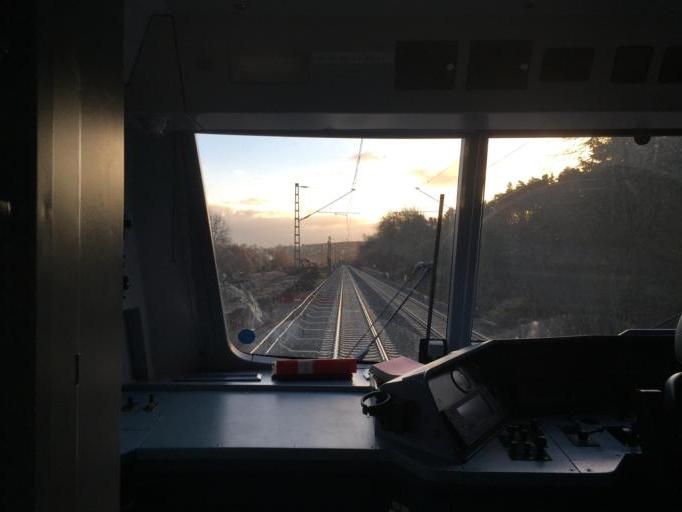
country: DE
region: Hesse
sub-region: Regierungsbezirk Darmstadt
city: Bad Vilbel
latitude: 50.1783
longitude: 8.7164
